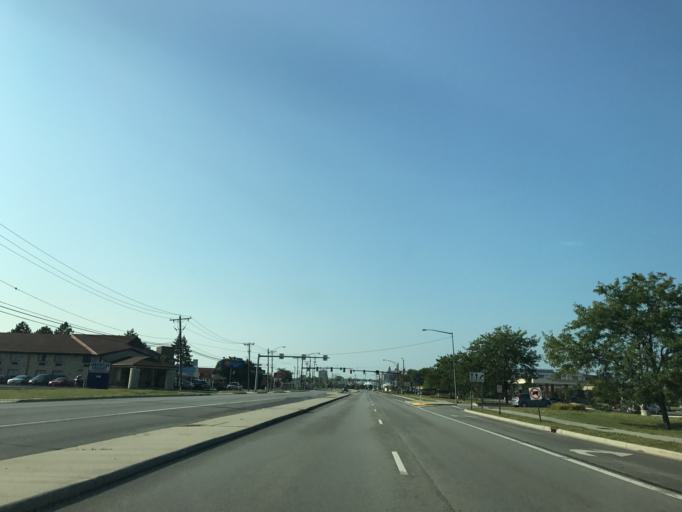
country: US
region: Ohio
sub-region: Lucas County
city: Maumee
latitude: 41.5852
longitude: -83.6650
